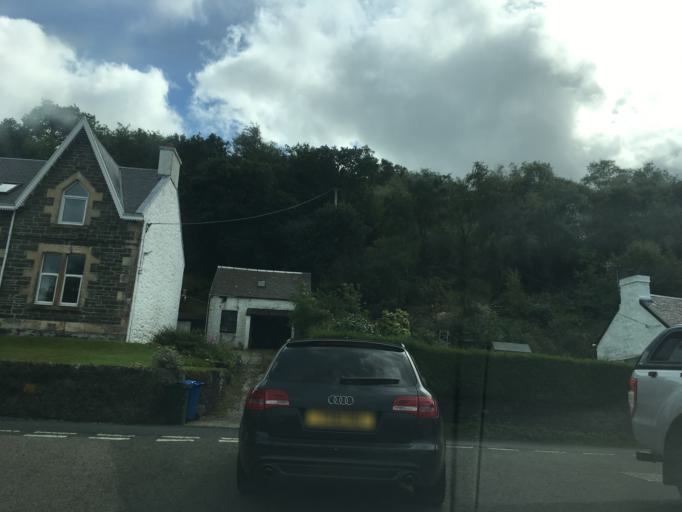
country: GB
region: Scotland
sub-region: Argyll and Bute
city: Tarbert
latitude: 55.8660
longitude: -5.4039
